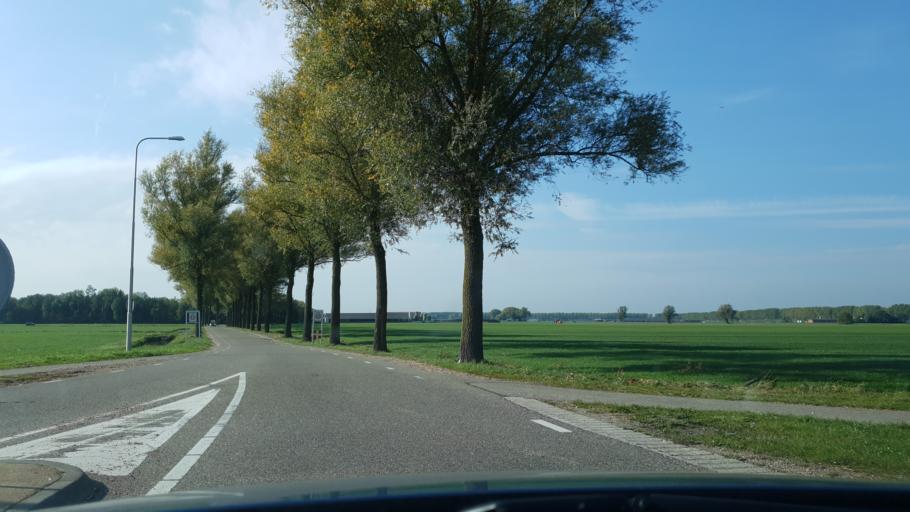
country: NL
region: Gelderland
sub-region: Gemeente Wijchen
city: Wijchen
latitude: 51.8402
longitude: 5.7371
